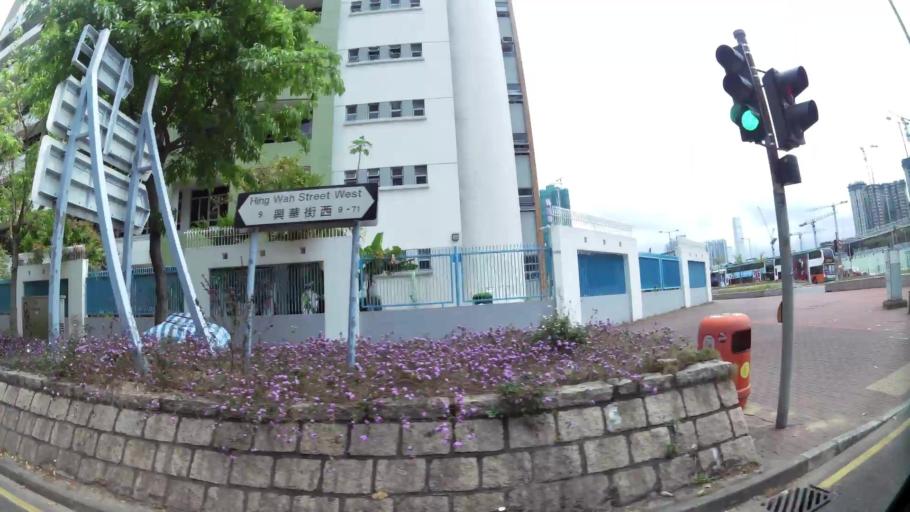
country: HK
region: Sham Shui Po
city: Sham Shui Po
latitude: 22.3319
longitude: 114.1491
